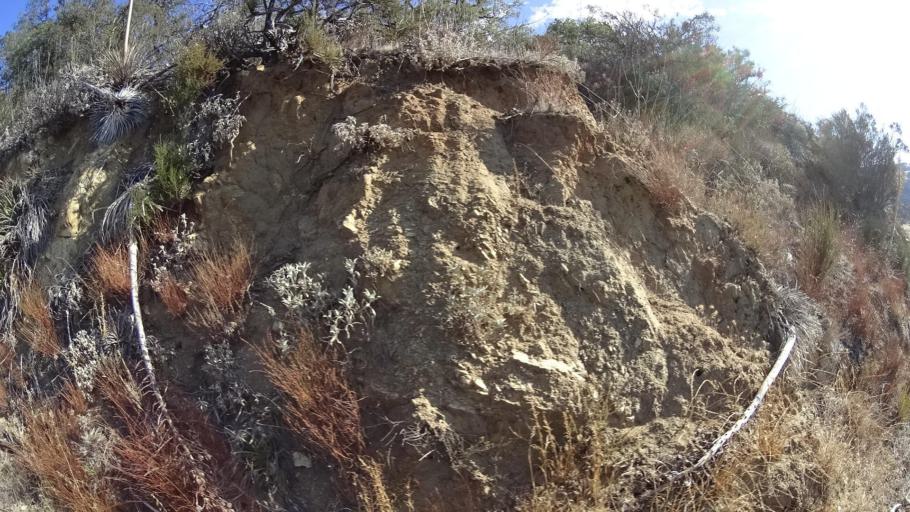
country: US
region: California
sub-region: San Diego County
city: Julian
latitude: 33.1468
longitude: -116.6991
